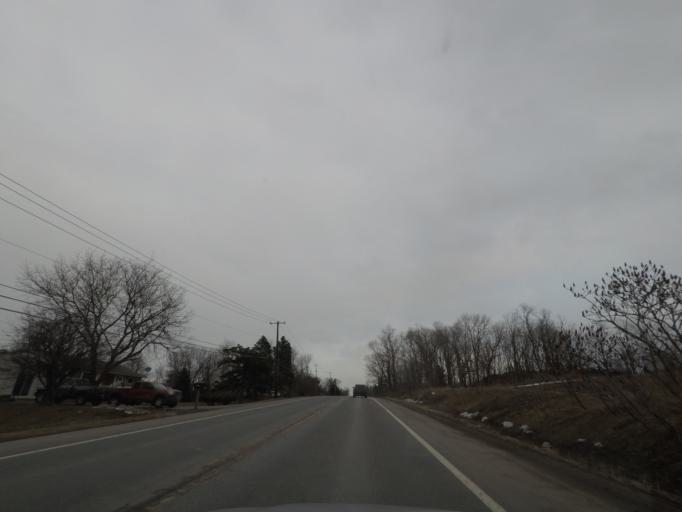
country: US
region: New York
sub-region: Madison County
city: Wampsville
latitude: 43.0768
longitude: -75.6793
